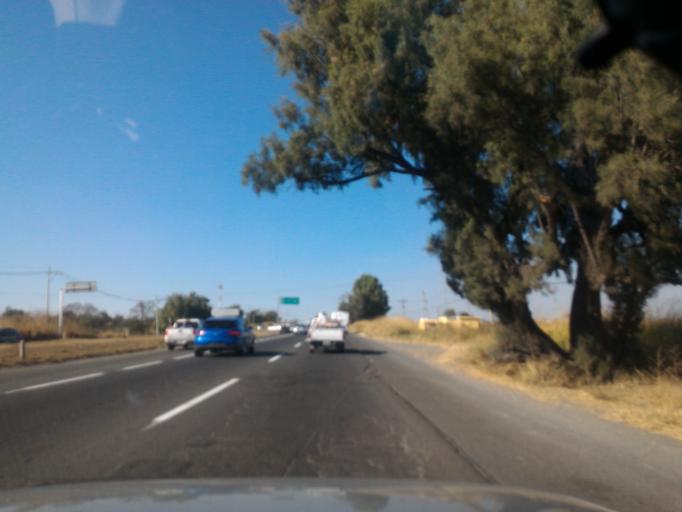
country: MX
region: Jalisco
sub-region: Ixtlahuacan de los Membrillos
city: Los Olivos
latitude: 20.4249
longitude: -103.2377
